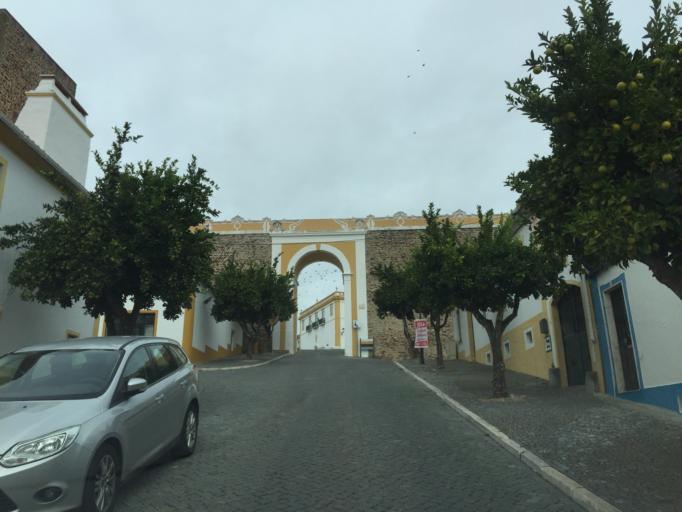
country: PT
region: Portalegre
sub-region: Avis
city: Avis
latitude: 39.0555
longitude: -7.8897
